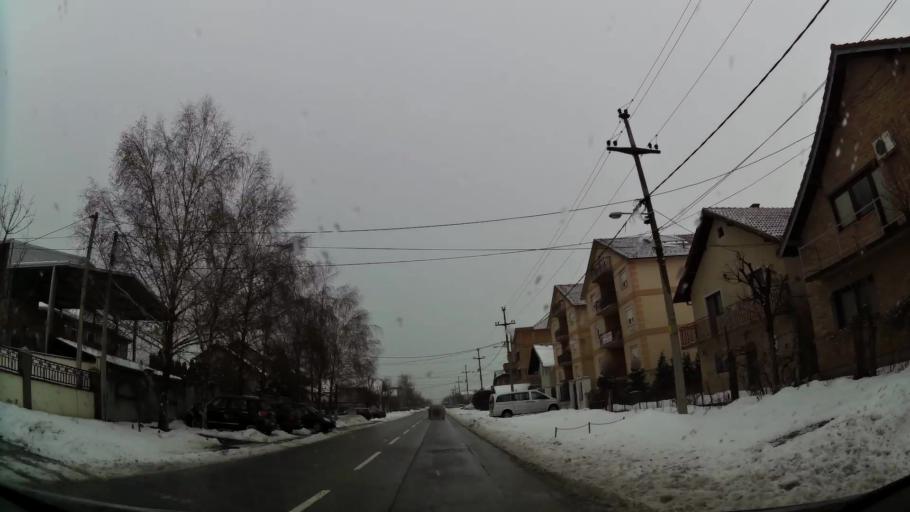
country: RS
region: Central Serbia
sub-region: Belgrade
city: Zemun
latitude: 44.8488
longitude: 20.3407
